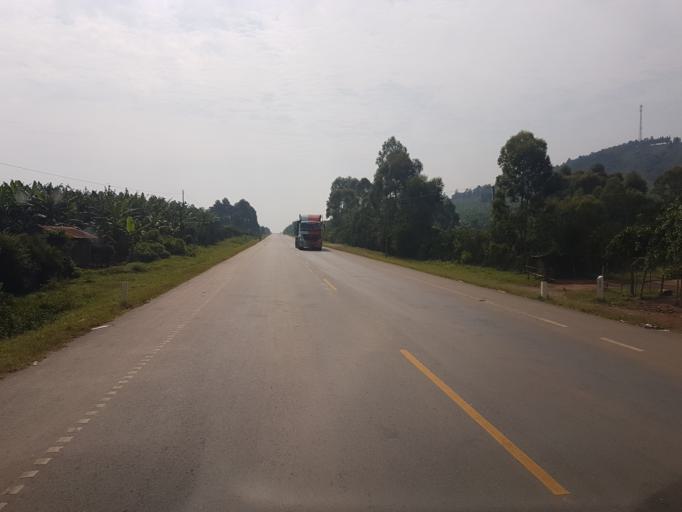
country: UG
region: Western Region
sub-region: Sheema District
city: Kibingo
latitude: -0.6401
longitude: 30.5081
